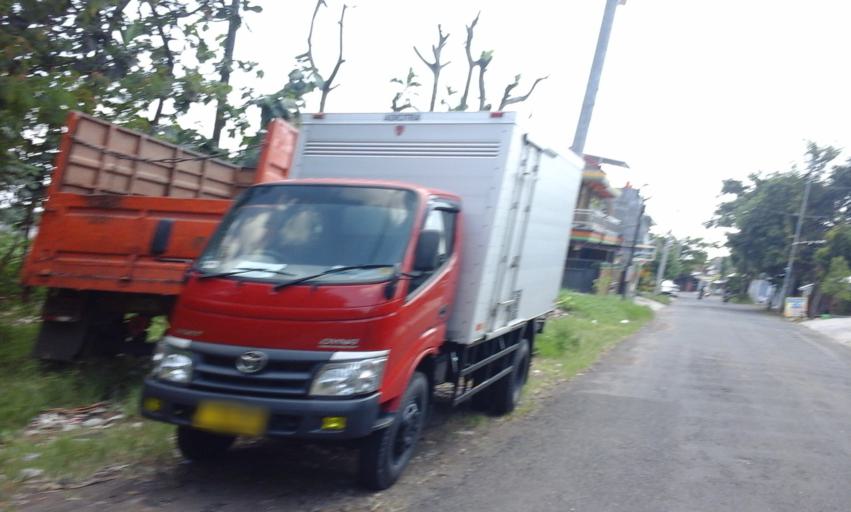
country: ID
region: East Java
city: Kaliwates
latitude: -8.1706
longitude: 113.6792
